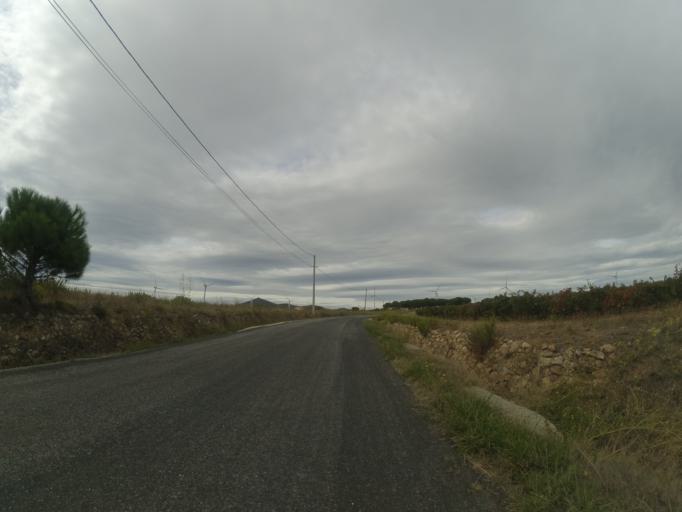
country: FR
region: Languedoc-Roussillon
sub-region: Departement des Pyrenees-Orientales
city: Pezilla-la-Riviere
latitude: 42.7067
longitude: 2.7605
